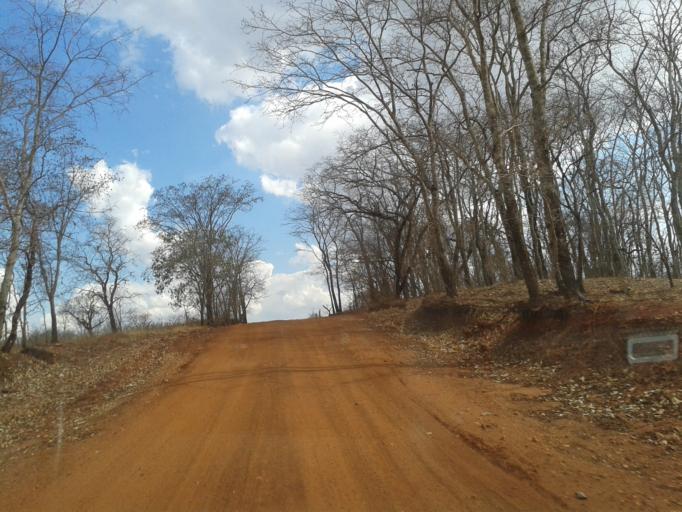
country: BR
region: Minas Gerais
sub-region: Santa Vitoria
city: Santa Vitoria
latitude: -19.2606
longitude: -49.9852
